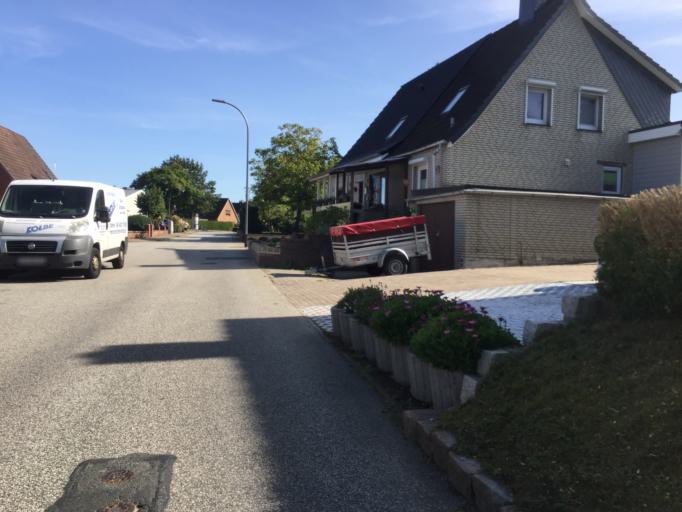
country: DE
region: Schleswig-Holstein
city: Itzehoe
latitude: 53.9080
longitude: 9.4959
